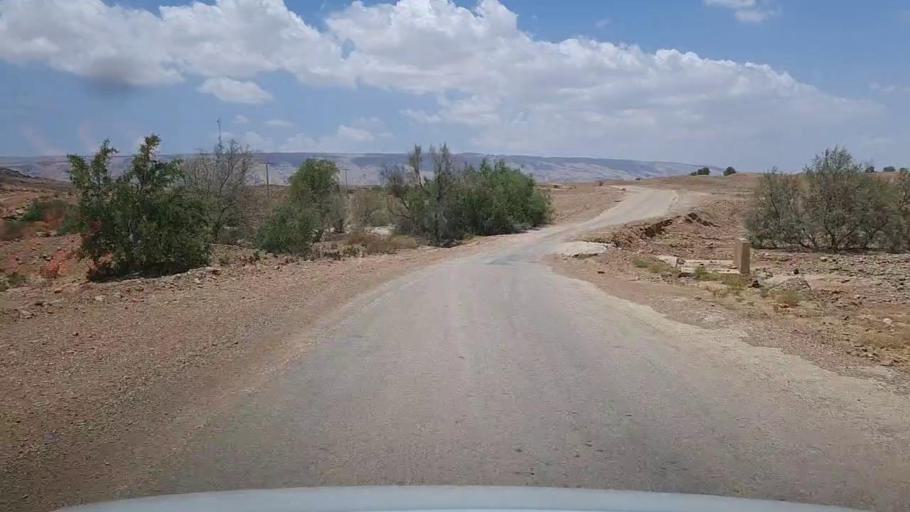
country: PK
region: Sindh
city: Bhan
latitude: 26.3190
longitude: 67.5556
